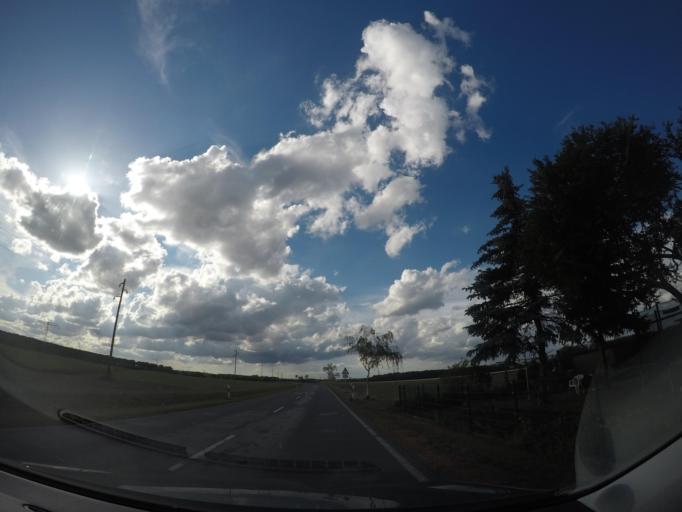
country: DE
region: Saxony-Anhalt
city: Haldensleben I
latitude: 52.3012
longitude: 11.3927
